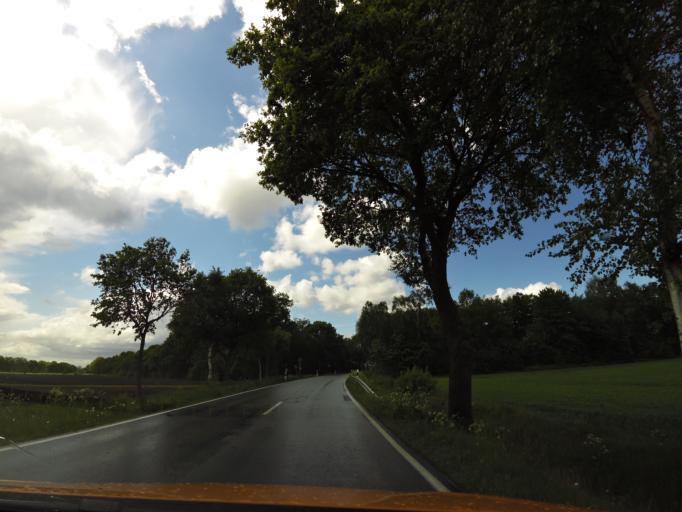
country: DE
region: Lower Saxony
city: Oldenburg
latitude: 53.1257
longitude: 8.3067
